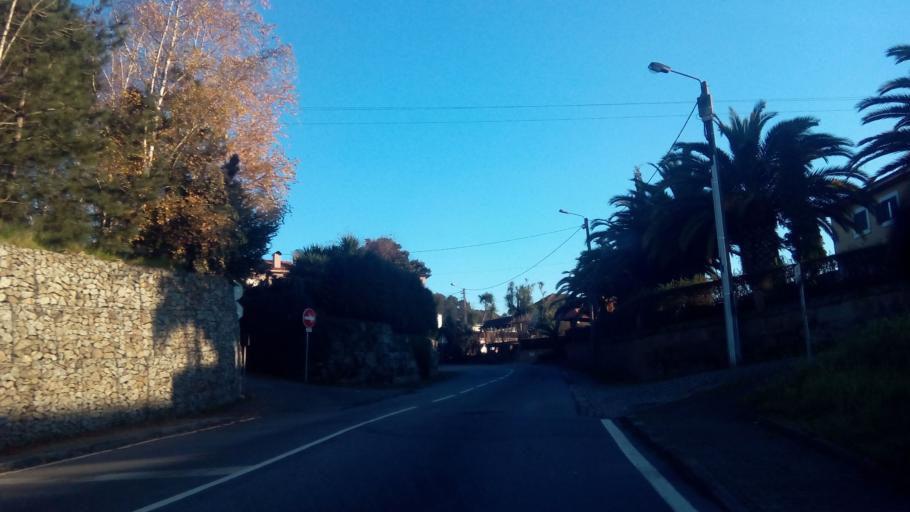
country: PT
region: Porto
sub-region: Penafiel
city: Penafiel
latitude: 41.2200
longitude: -8.2907
